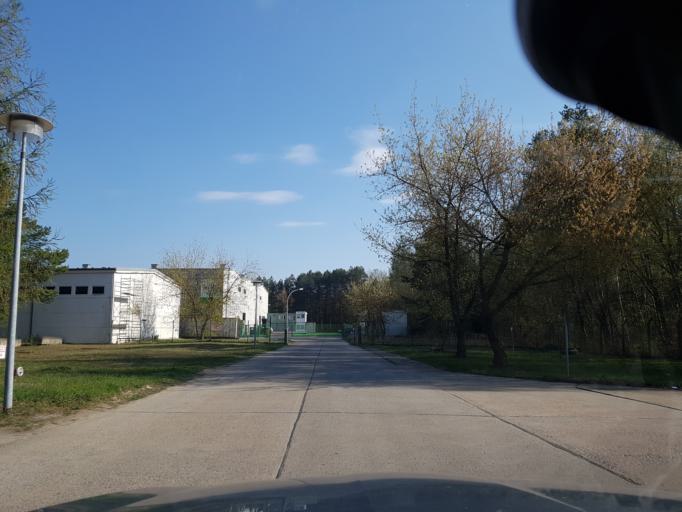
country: DE
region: Brandenburg
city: Schonborn
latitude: 51.6283
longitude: 13.5156
